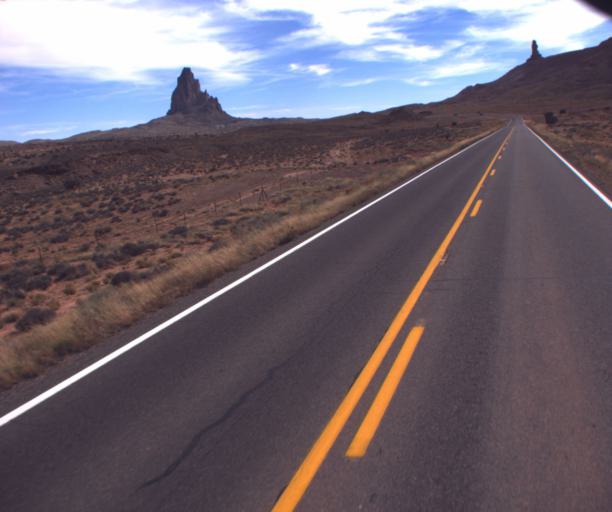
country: US
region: Arizona
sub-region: Navajo County
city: Kayenta
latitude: 36.8442
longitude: -110.2676
